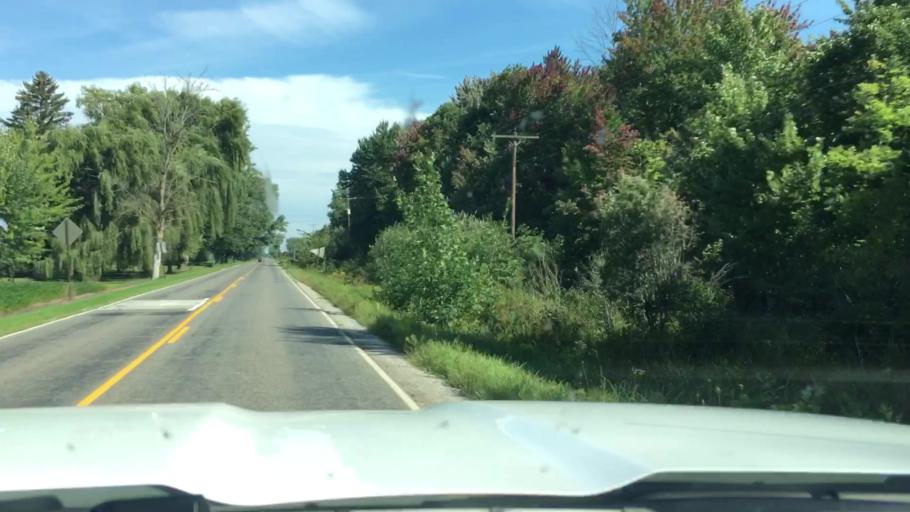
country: US
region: Michigan
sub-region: Saginaw County
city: Hemlock
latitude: 43.4843
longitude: -84.2300
